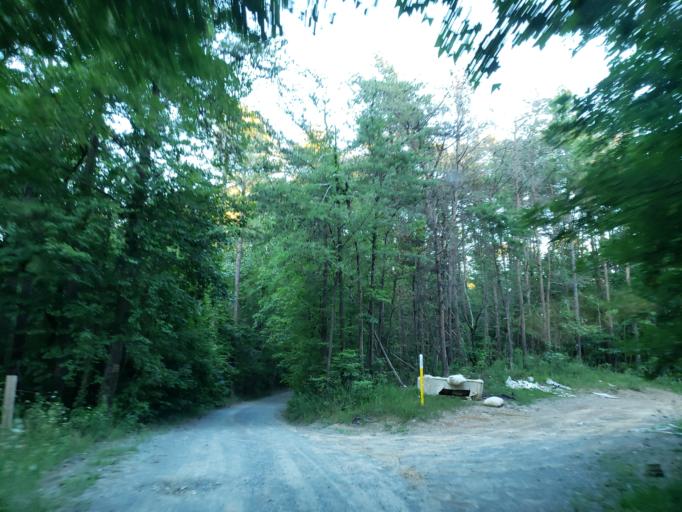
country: US
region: Georgia
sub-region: Bartow County
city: Euharlee
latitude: 34.0835
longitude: -84.8658
